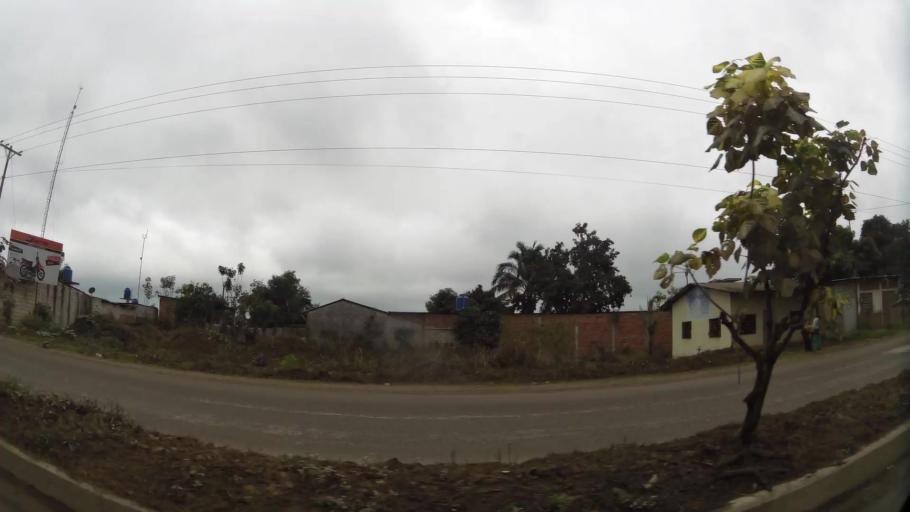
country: EC
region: El Oro
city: Pasaje
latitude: -3.3290
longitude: -79.7801
